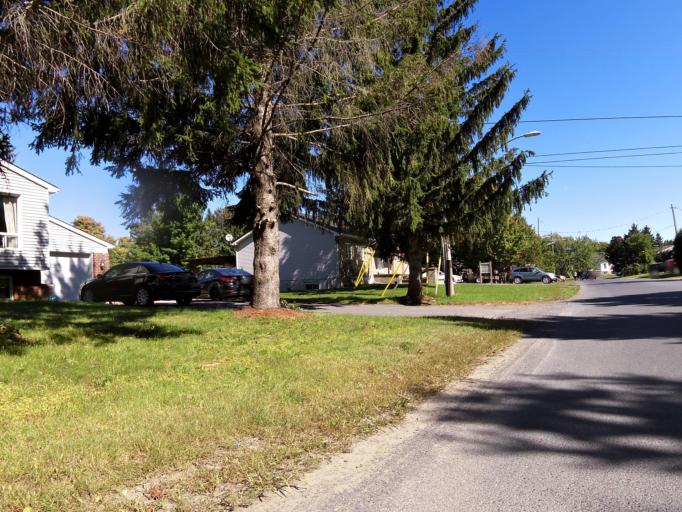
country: CA
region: Ontario
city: Casselman
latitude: 45.2660
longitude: -75.2800
